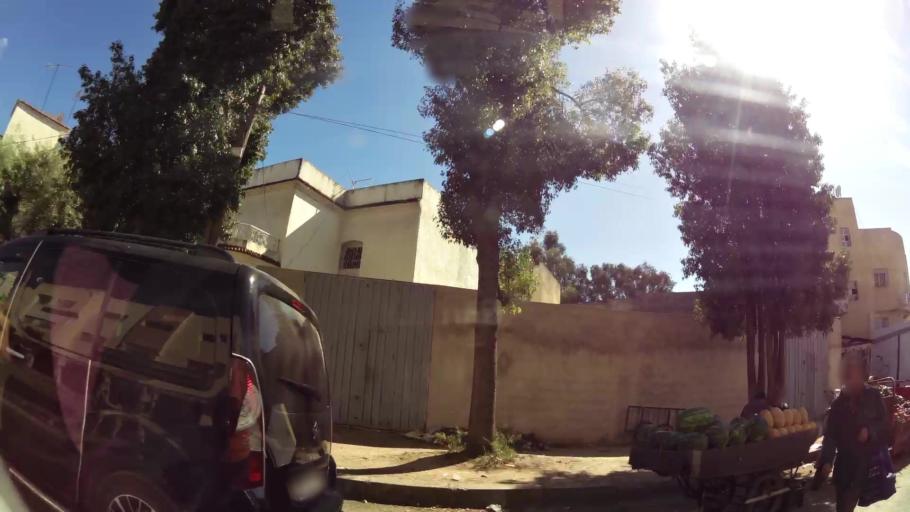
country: MA
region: Fes-Boulemane
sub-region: Fes
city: Fes
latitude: 34.0195
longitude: -4.9853
